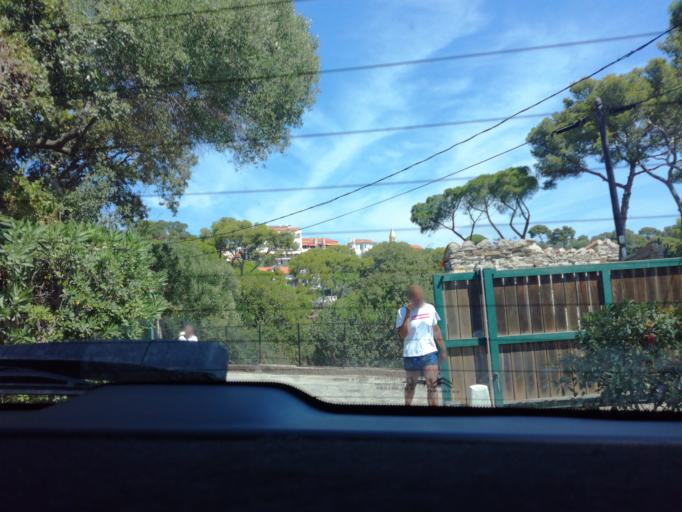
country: FR
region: Provence-Alpes-Cote d'Azur
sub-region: Departement du Var
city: Carqueiranne
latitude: 43.0360
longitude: 6.1306
